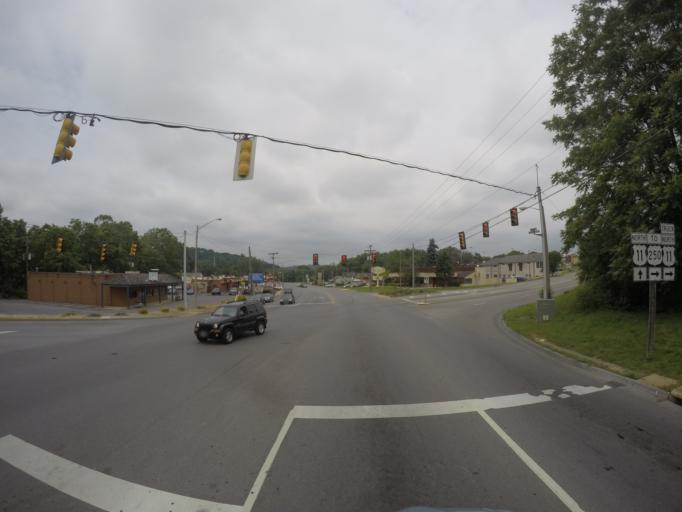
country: US
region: Virginia
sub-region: City of Staunton
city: Staunton
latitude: 38.1366
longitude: -79.0667
